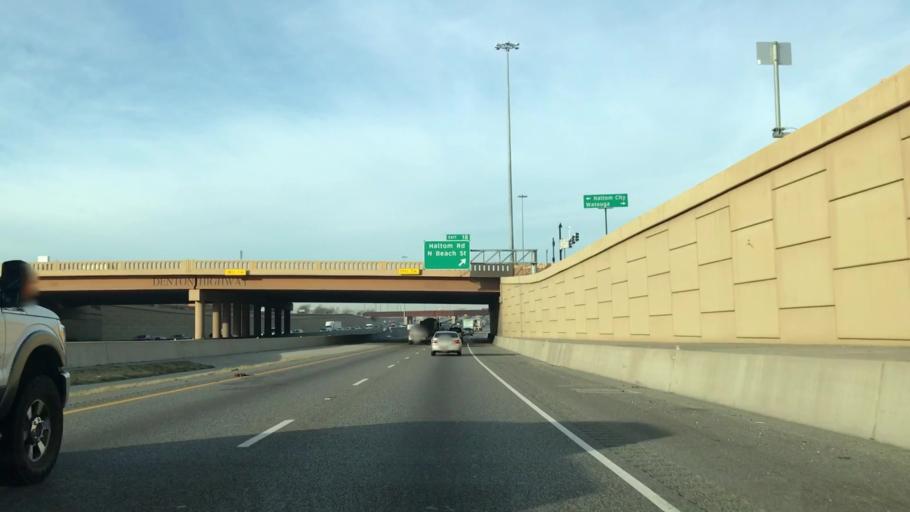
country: US
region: Texas
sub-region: Tarrant County
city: Watauga
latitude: 32.8398
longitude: -97.2631
